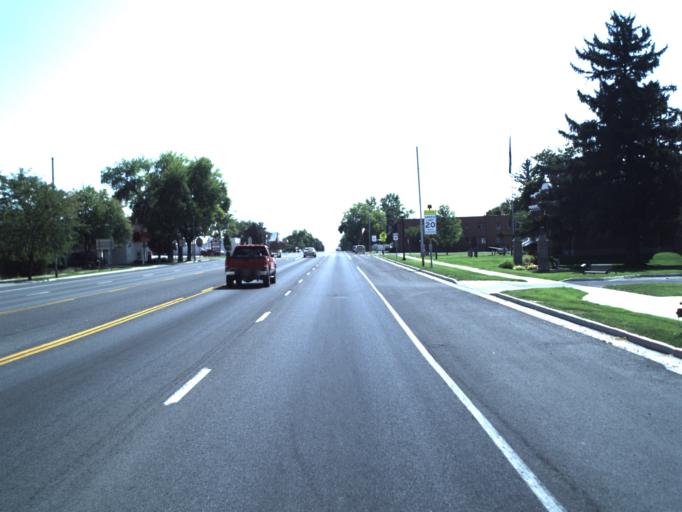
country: US
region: Utah
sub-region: Cache County
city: Smithfield
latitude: 41.8380
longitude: -111.8327
